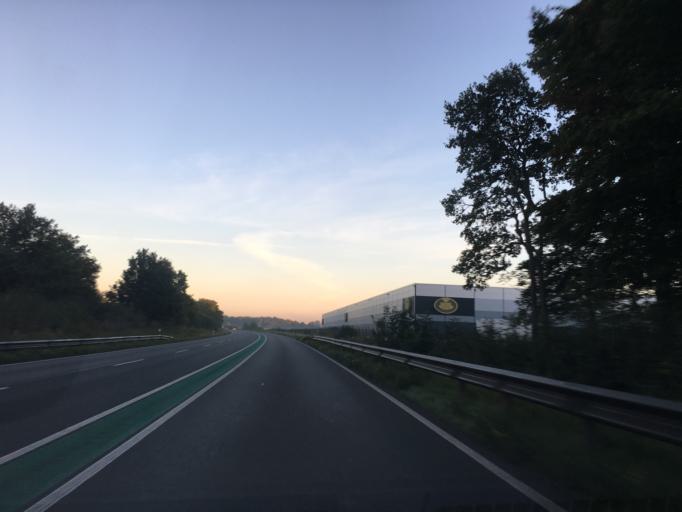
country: DE
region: North Rhine-Westphalia
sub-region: Regierungsbezirk Munster
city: Laer
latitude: 52.0907
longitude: 7.4140
